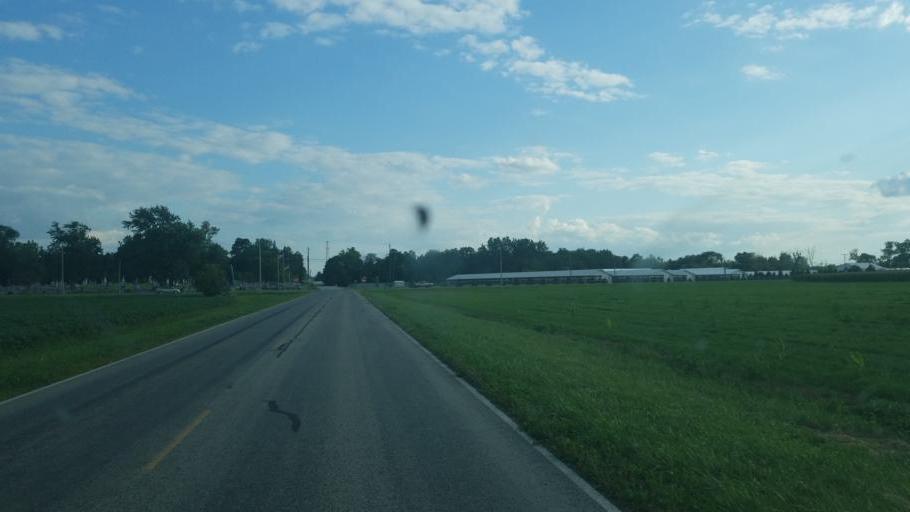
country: US
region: Ohio
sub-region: Seneca County
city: Tiffin
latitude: 41.1230
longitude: -83.1500
